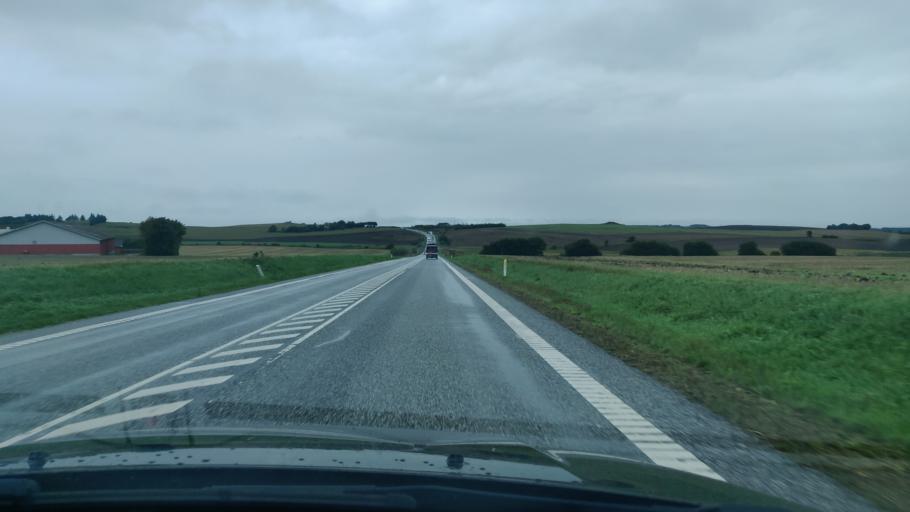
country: DK
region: North Denmark
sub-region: Thisted Kommune
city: Thisted
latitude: 56.9898
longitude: 8.7730
